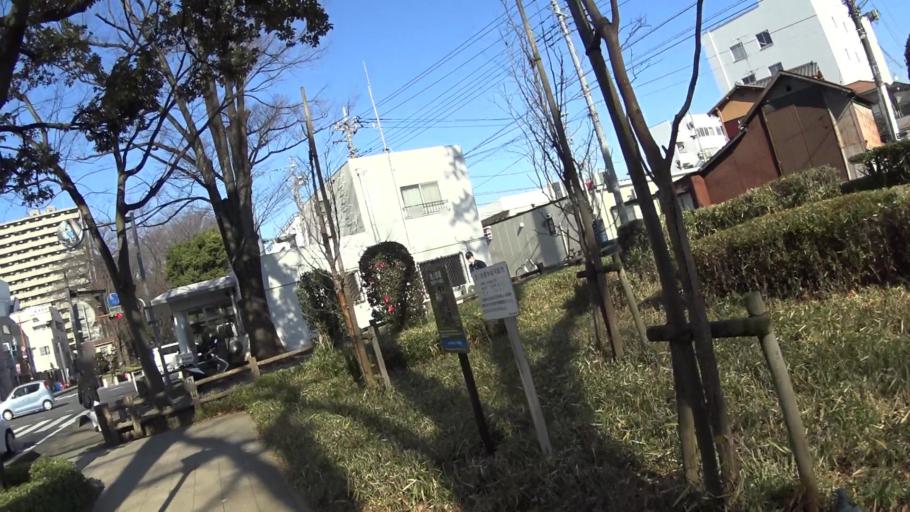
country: JP
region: Saitama
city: Yono
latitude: 35.9073
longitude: 139.6309
